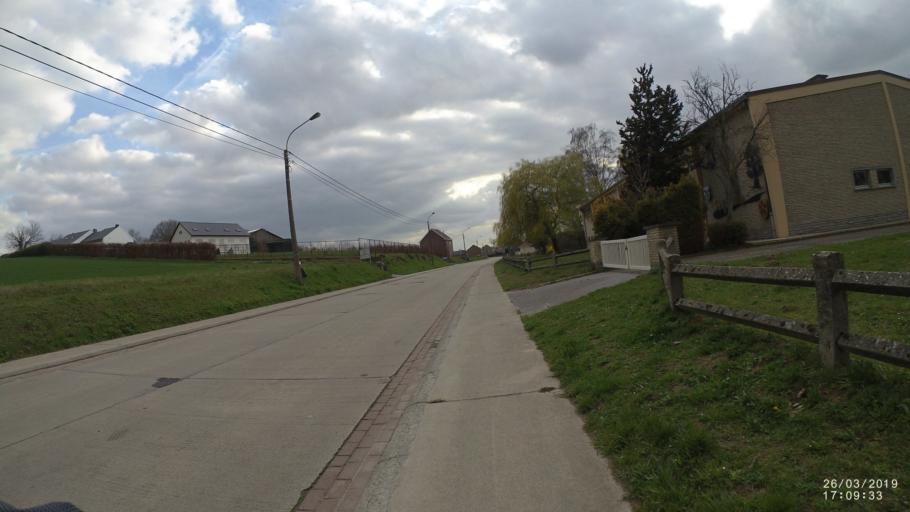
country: BE
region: Flanders
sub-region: Provincie Vlaams-Brabant
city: Huldenberg
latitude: 50.8394
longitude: 4.5773
